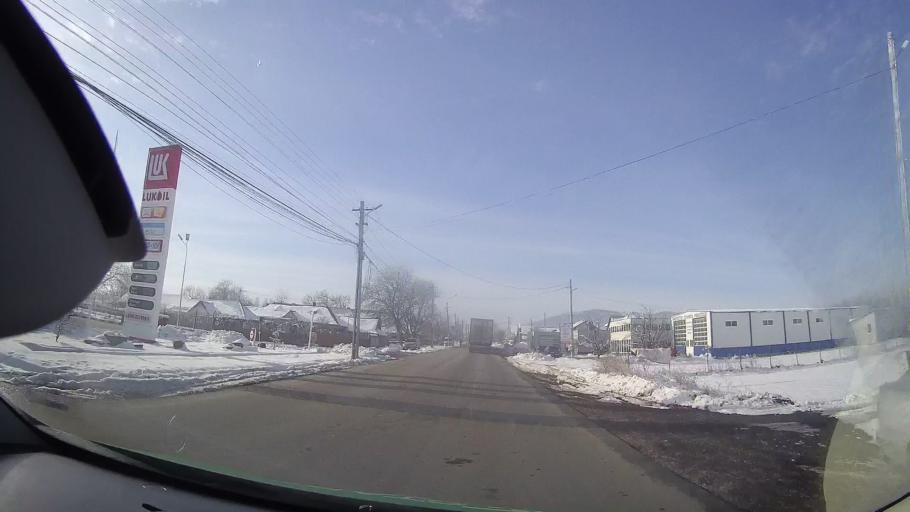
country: RO
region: Neamt
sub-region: Oras Targu Neamt
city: Targu Neamt
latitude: 47.2089
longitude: 26.3948
